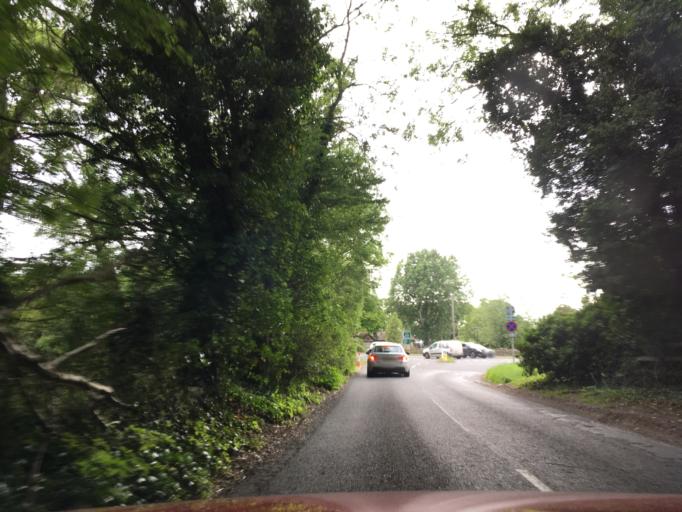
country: GB
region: England
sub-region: Oxfordshire
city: Boars Hill
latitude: 51.7132
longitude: -1.3339
